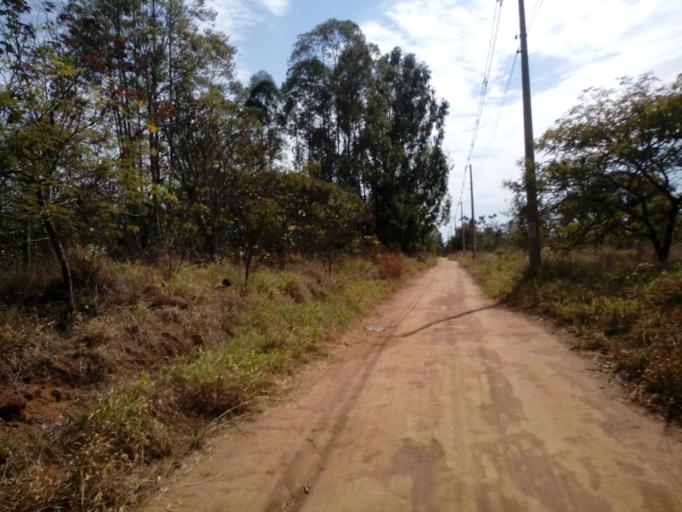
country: BR
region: Sao Paulo
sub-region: Sao Carlos
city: Sao Carlos
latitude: -21.9767
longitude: -47.8754
